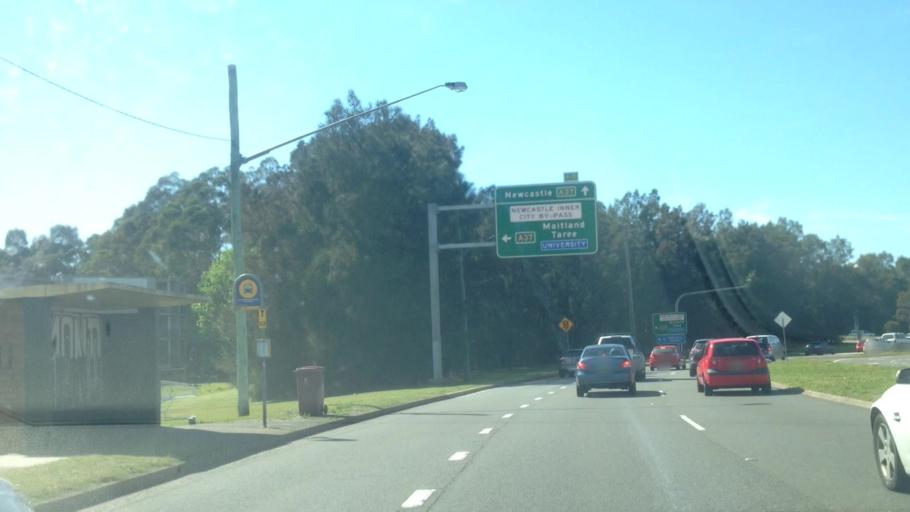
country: AU
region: New South Wales
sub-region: Newcastle
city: Lambton
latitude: -32.9048
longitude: 151.6908
